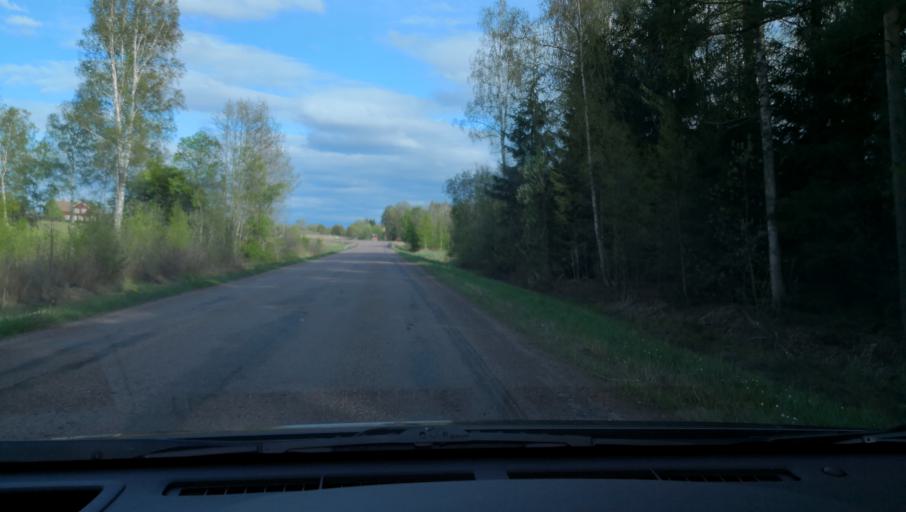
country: SE
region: Dalarna
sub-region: Saters Kommun
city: Saeter
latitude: 60.2984
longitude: 15.8562
